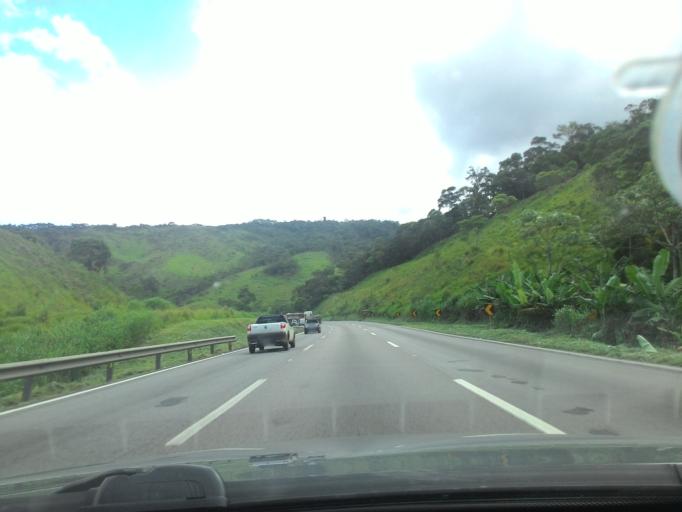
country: BR
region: Sao Paulo
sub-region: Cajati
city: Cajati
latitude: -24.8773
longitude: -48.2279
